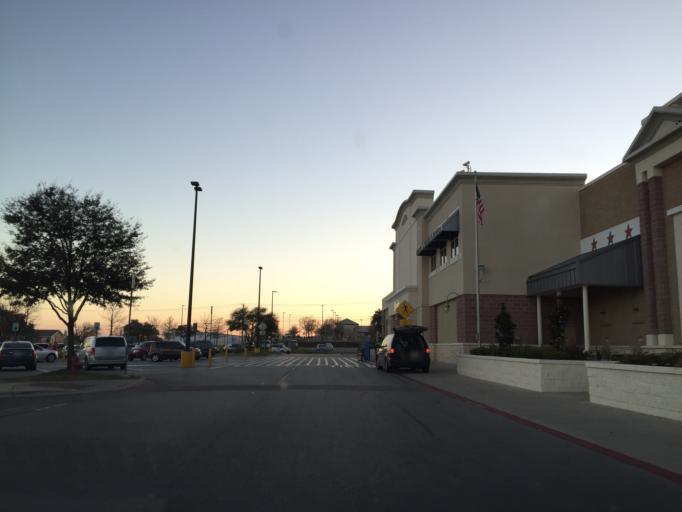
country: US
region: Texas
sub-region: Travis County
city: Pflugerville
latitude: 30.4533
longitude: -97.6064
